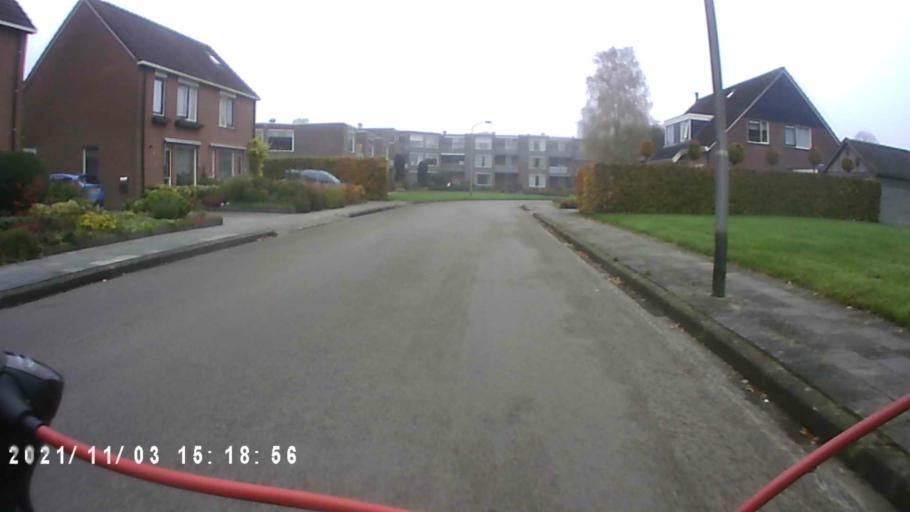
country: NL
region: Groningen
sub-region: Gemeente Leek
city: Leek
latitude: 53.1613
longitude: 6.3634
